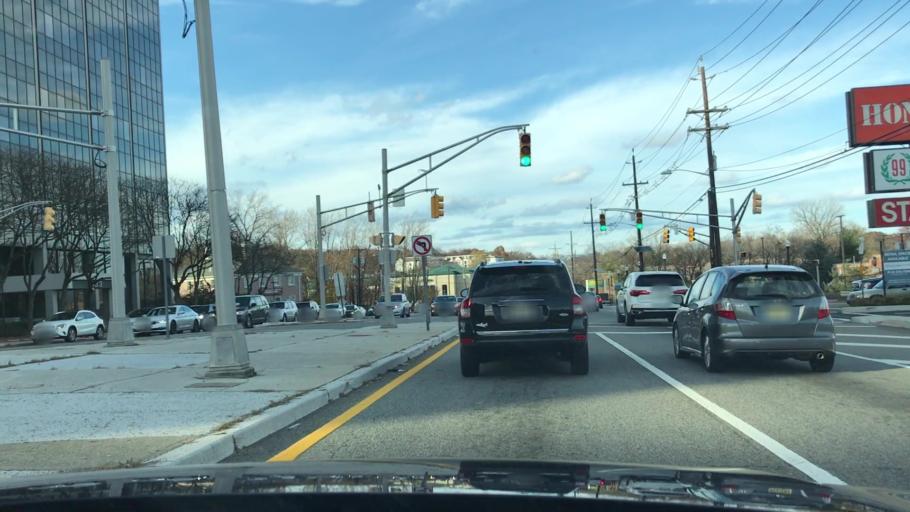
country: US
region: New Jersey
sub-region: Bergen County
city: River Edge
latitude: 40.9094
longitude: -74.0330
